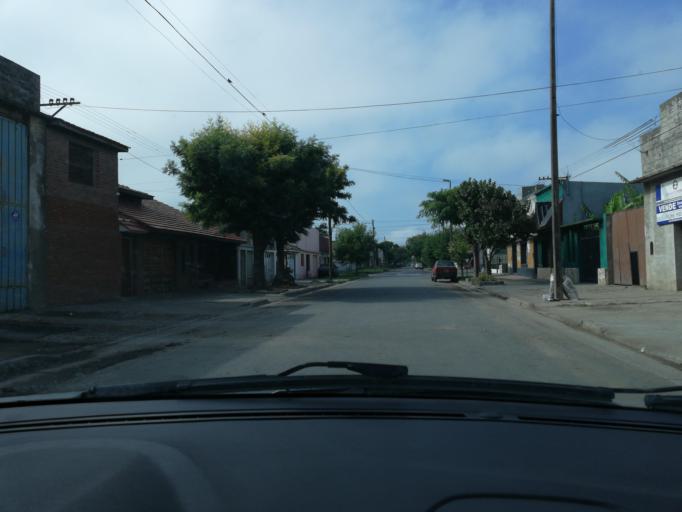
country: AR
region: Buenos Aires
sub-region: Partido de Balcarce
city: Balcarce
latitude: -37.8361
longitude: -58.2648
